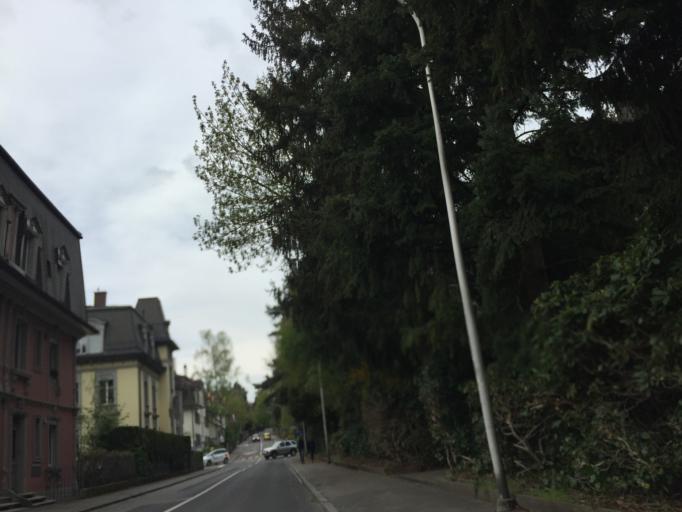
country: CH
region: Bern
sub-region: Bern-Mittelland District
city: Muri
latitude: 46.9358
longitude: 7.4659
